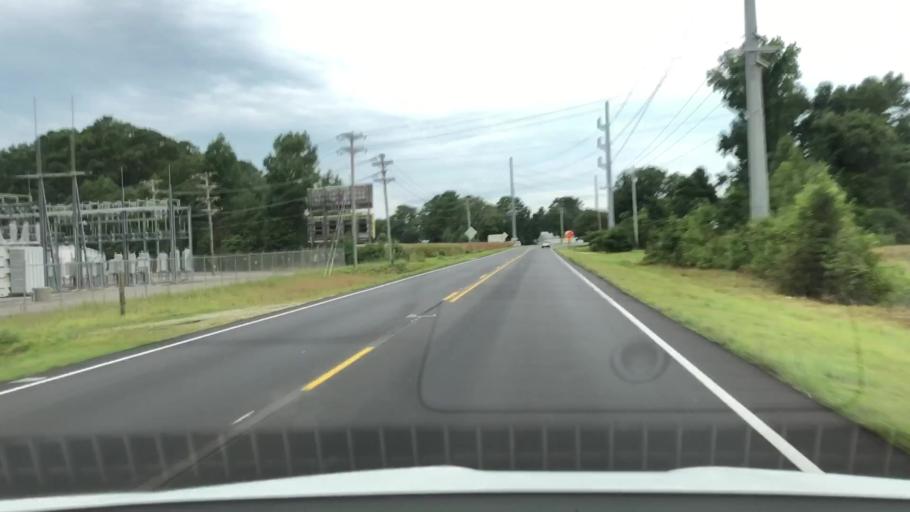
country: US
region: North Carolina
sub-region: Onslow County
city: Swansboro
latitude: 34.7888
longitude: -77.1260
